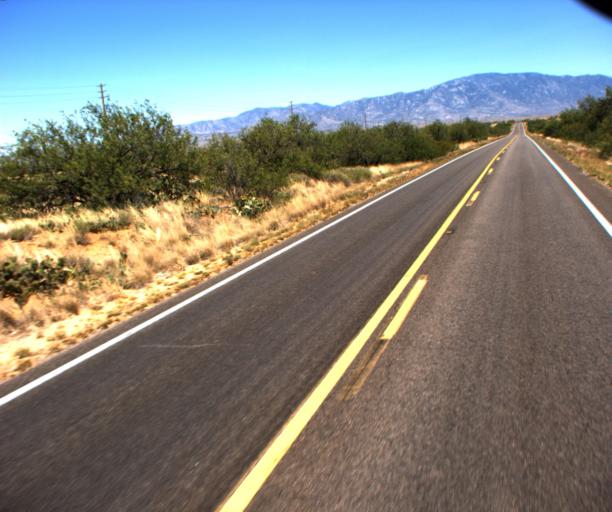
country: US
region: Arizona
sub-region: Pima County
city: Catalina
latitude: 32.6007
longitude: -110.9798
